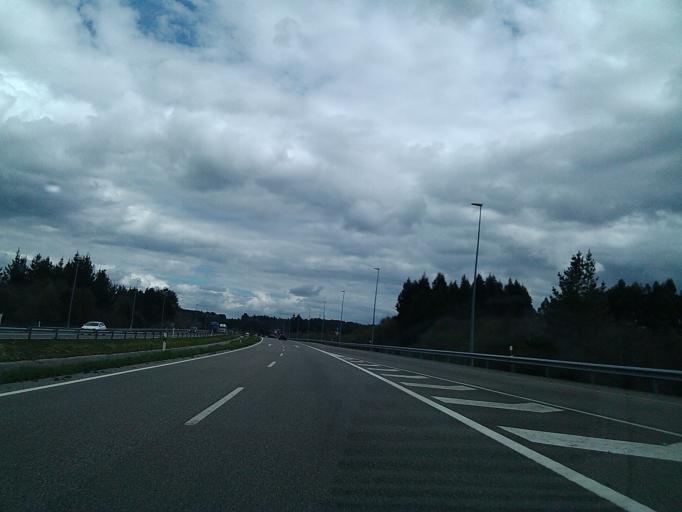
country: ES
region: Galicia
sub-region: Provincia de Lugo
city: Guitiriz
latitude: 43.1877
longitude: -7.9240
